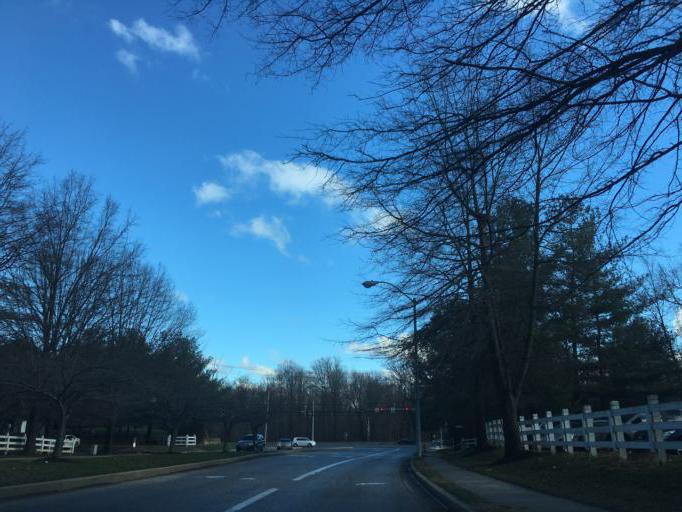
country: US
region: Maryland
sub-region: Baltimore County
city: Owings Mills
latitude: 39.3980
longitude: -76.7876
